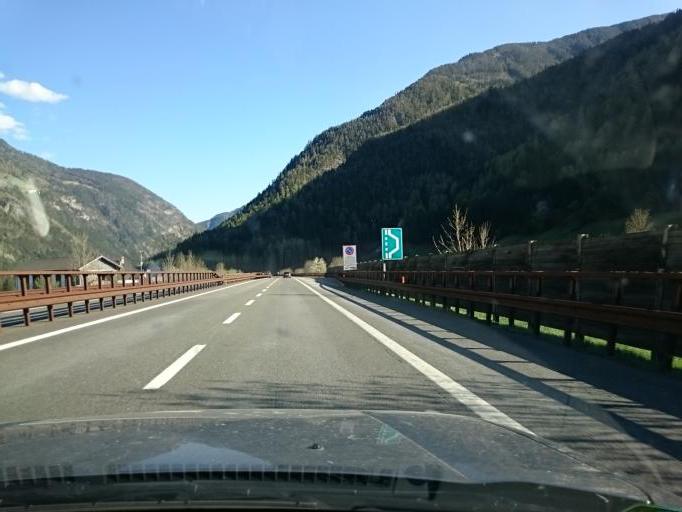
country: IT
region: Trentino-Alto Adige
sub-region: Bolzano
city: Campo di Trens
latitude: 46.8502
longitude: 11.5138
